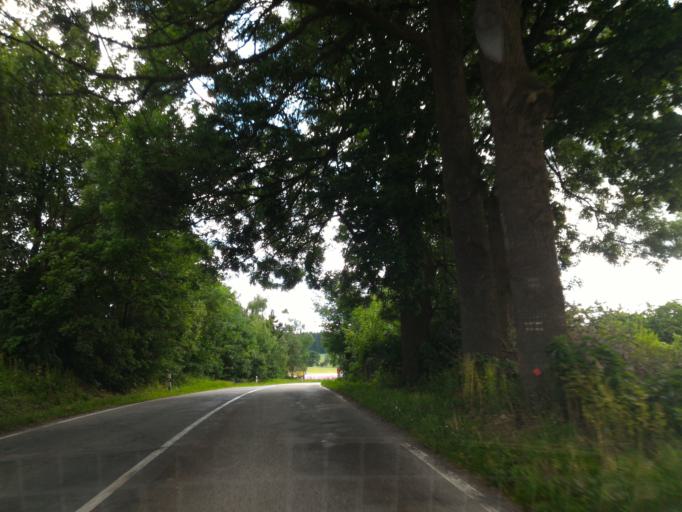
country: CZ
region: Vysocina
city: Bohdalov
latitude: 49.4581
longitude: 15.8058
